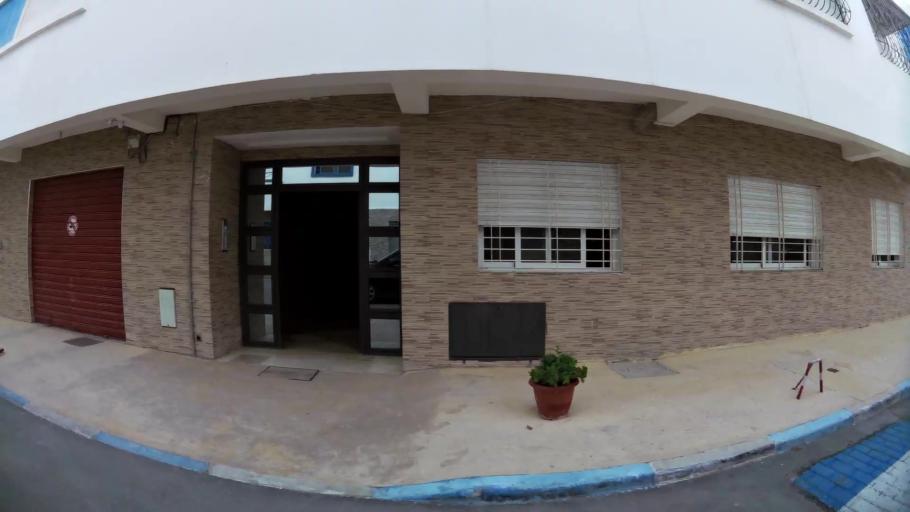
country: MA
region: Tanger-Tetouan
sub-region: Tetouan
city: Martil
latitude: 35.6103
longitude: -5.2826
